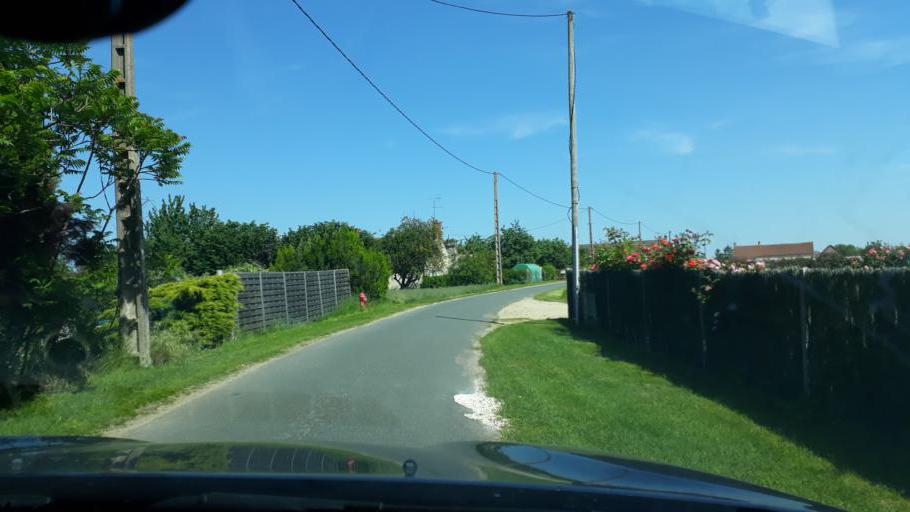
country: FR
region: Centre
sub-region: Departement du Loiret
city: Saint-Benoit-sur-Loire
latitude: 47.8073
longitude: 2.2604
